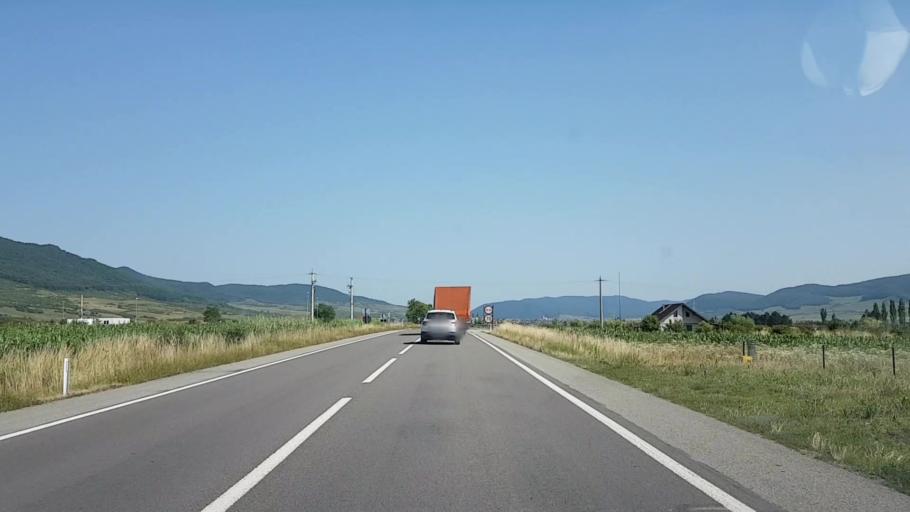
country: RO
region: Bistrita-Nasaud
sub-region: Comuna Sieu-Magherus
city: Sieu-Magherus
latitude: 47.1082
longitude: 24.3482
